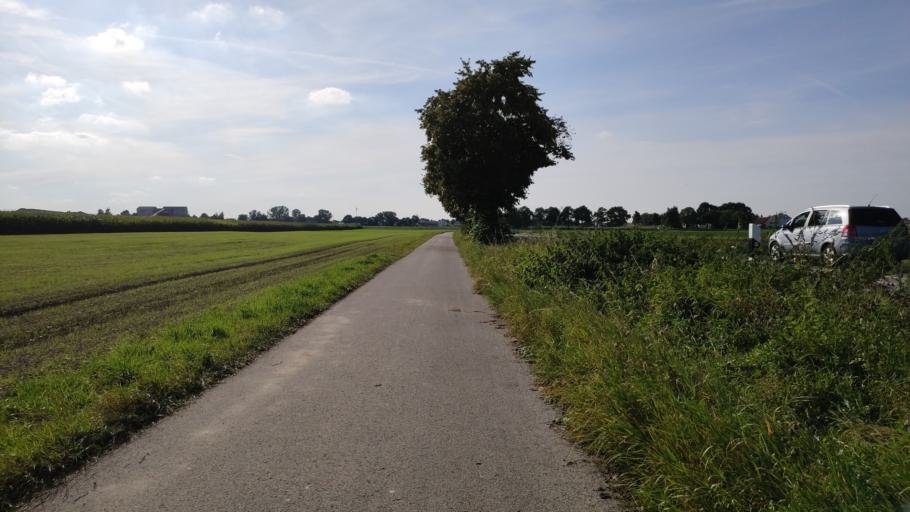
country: DE
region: Bavaria
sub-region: Swabia
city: Konigsbrunn
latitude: 48.2508
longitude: 10.8907
